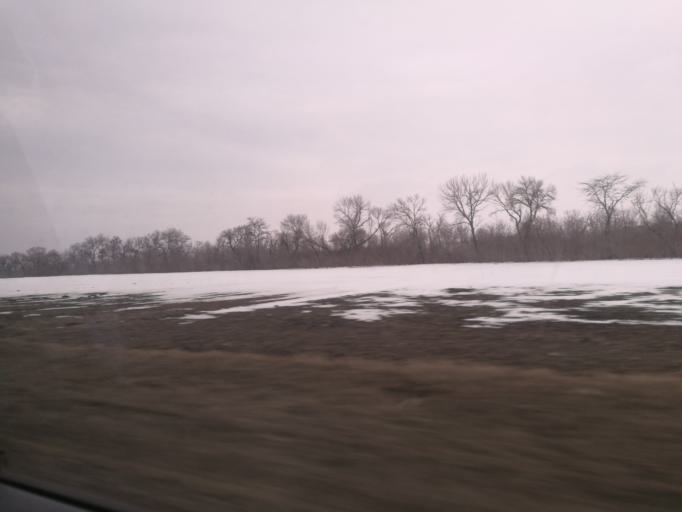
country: RO
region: Iasi
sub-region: Comuna Ruginoasa
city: Rediu
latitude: 47.2448
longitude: 26.8779
